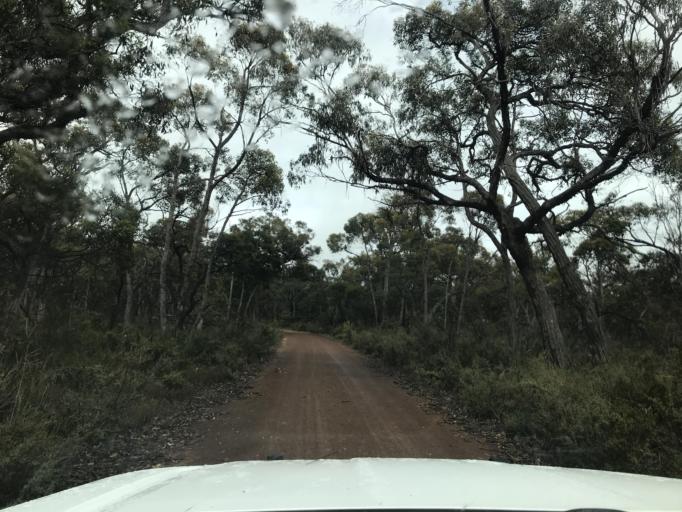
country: AU
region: South Australia
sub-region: Wattle Range
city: Penola
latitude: -37.2595
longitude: 141.3338
